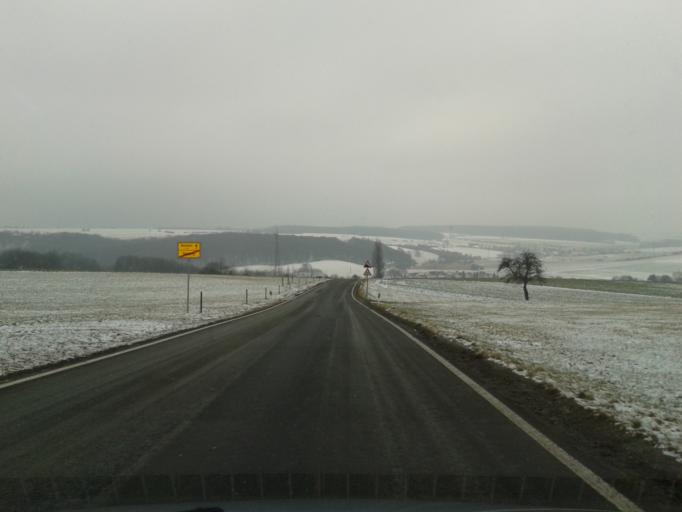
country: DE
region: Thuringia
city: Hainichen
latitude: 50.9971
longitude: 11.6006
